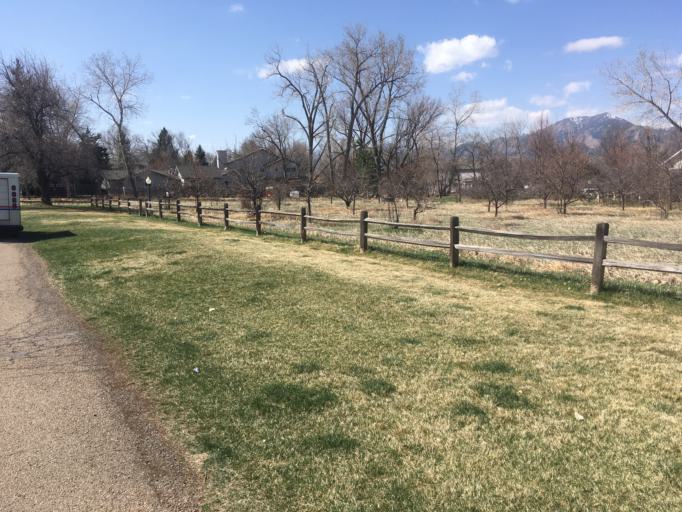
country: US
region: Colorado
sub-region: Boulder County
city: Boulder
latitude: 40.0081
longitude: -105.2067
